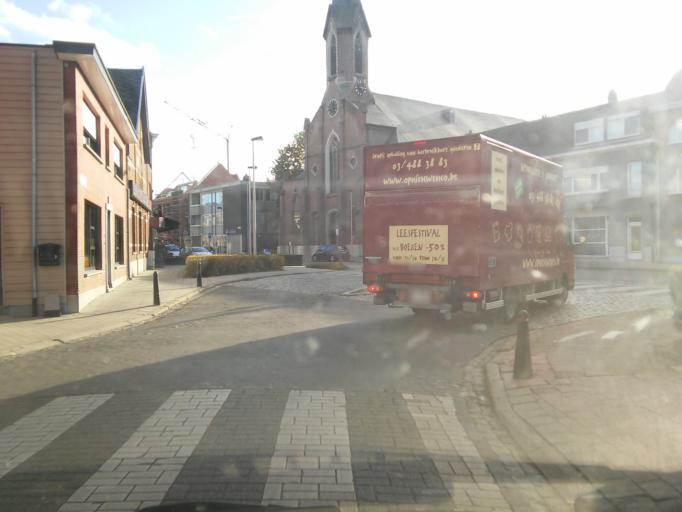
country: BE
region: Flanders
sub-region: Provincie Antwerpen
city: Putte
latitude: 51.0954
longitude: 4.6104
